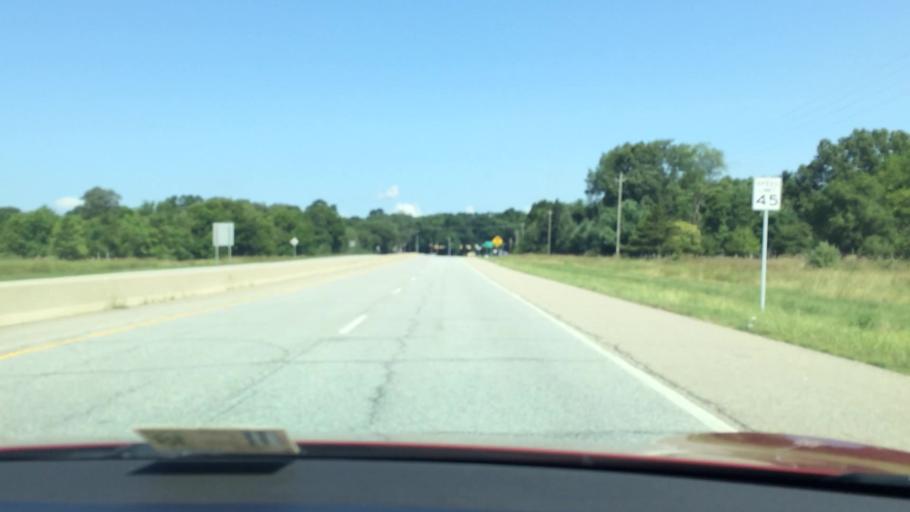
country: US
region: Indiana
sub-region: Saint Joseph County
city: Granger
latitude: 41.7338
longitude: -86.1489
